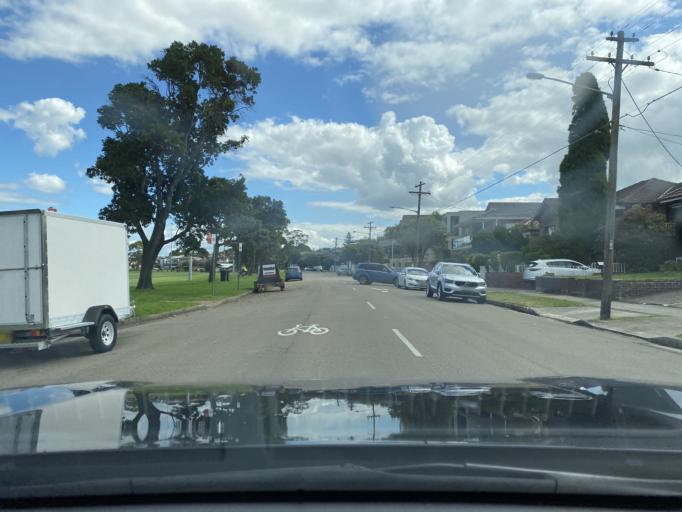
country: AU
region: New South Wales
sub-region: Canada Bay
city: Wareemba
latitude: -33.8684
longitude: 151.1407
